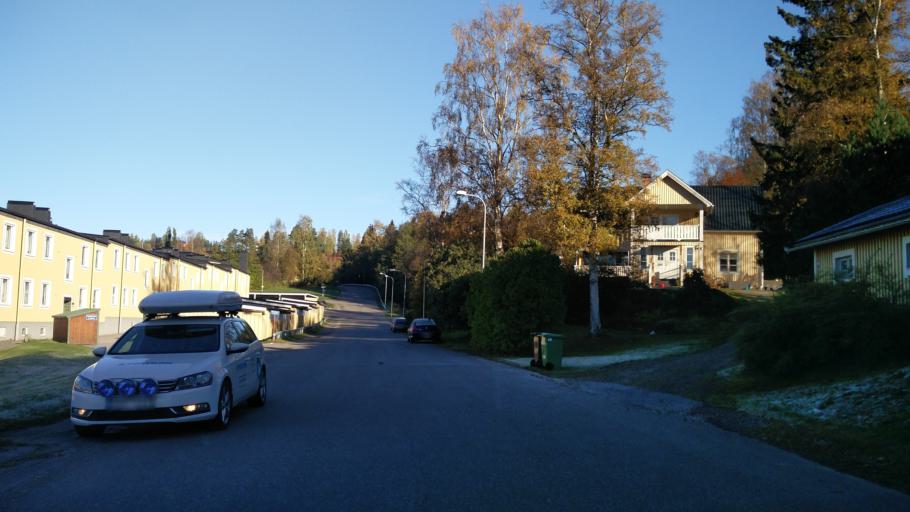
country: SE
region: Vaesternorrland
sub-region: Sundsvalls Kommun
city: Sundsvall
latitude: 62.4033
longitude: 17.2660
